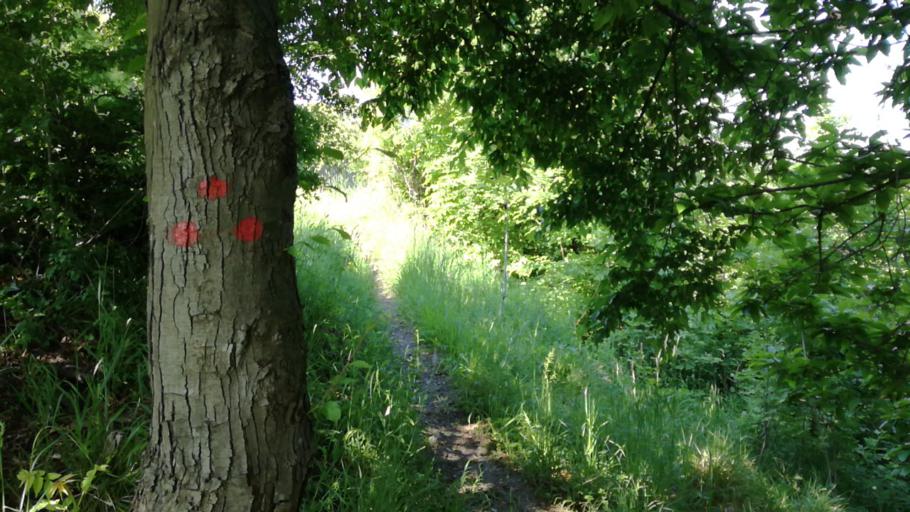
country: IT
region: Liguria
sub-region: Provincia di Genova
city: San Teodoro
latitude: 44.4249
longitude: 8.8997
